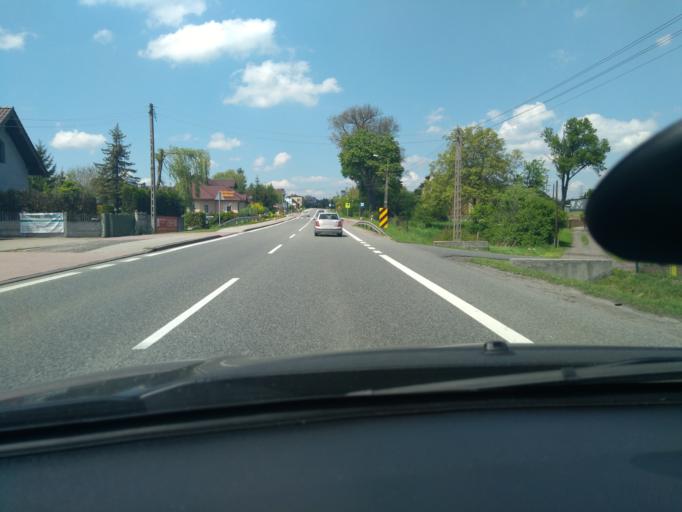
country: PL
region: Silesian Voivodeship
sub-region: Powiat mikolowski
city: Mikolow
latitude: 50.1836
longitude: 18.8785
